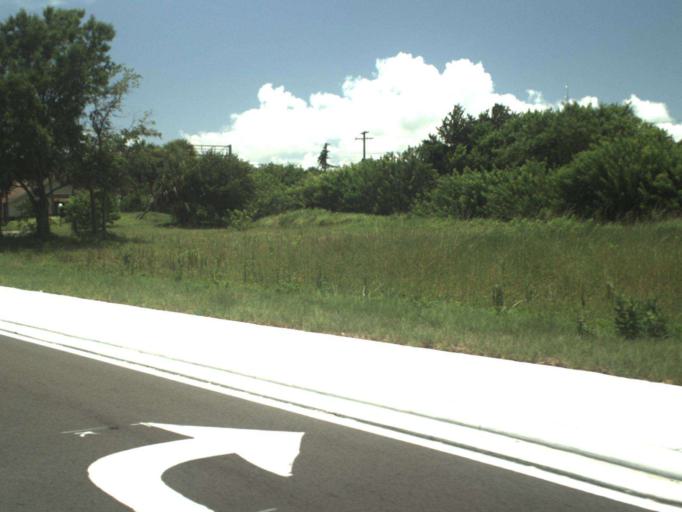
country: US
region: Florida
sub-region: Indian River County
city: Florida Ridge
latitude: 27.5671
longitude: -80.3712
